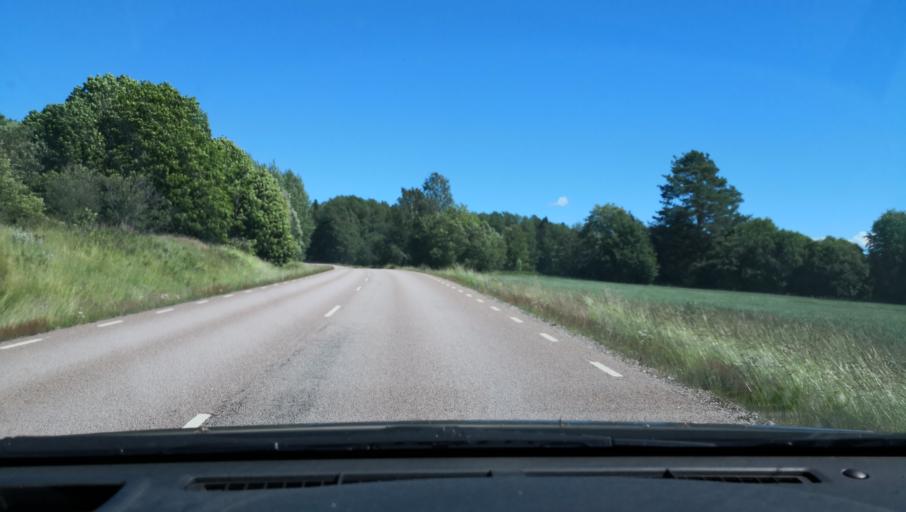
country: SE
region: Vaestmanland
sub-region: Kungsors Kommun
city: Kungsoer
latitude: 59.2885
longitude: 16.1033
